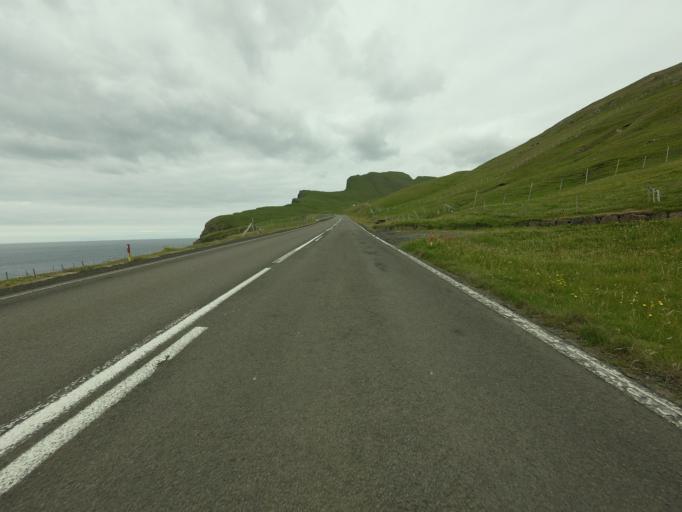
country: FO
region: Suduroy
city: Vagur
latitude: 61.4081
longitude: -6.7335
